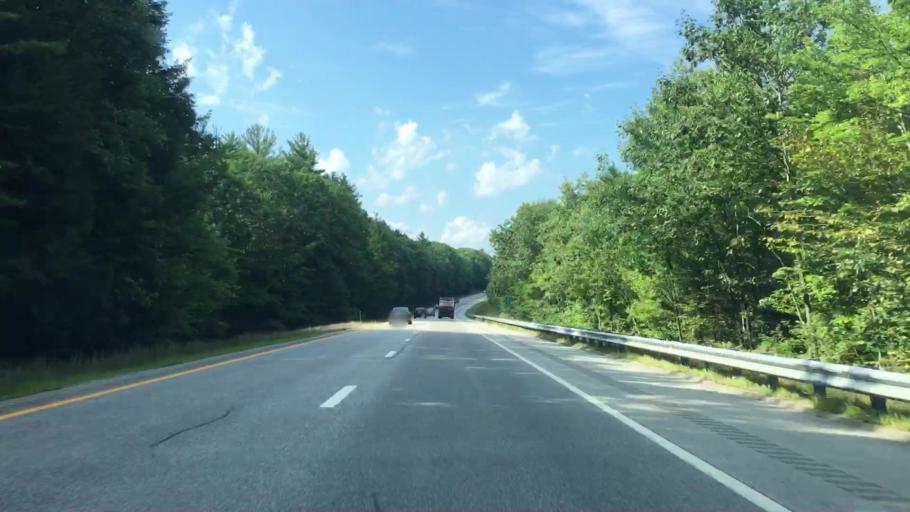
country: US
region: New Hampshire
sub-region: Belknap County
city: Sanbornton
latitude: 43.4826
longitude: -71.5907
